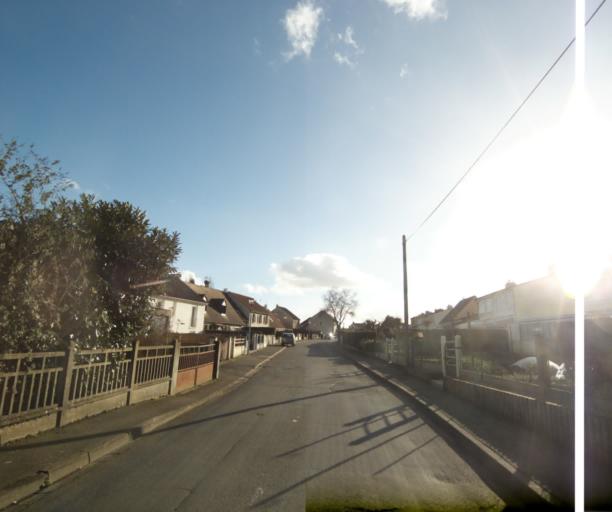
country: FR
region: Pays de la Loire
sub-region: Departement de la Sarthe
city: Le Mans
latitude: 48.0031
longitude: 0.1719
